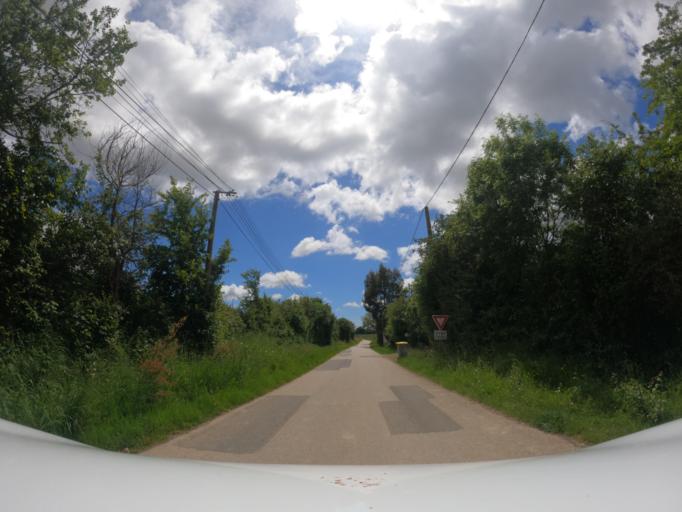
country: FR
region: Pays de la Loire
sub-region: Departement de la Vendee
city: Le Champ-Saint-Pere
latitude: 46.4864
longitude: -1.3580
